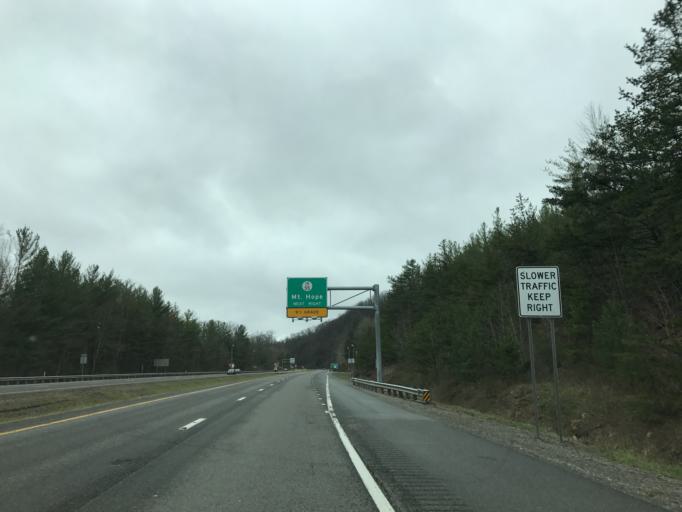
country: US
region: West Virginia
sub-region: Fayette County
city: Mount Hope
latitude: 37.8937
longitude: -81.1841
